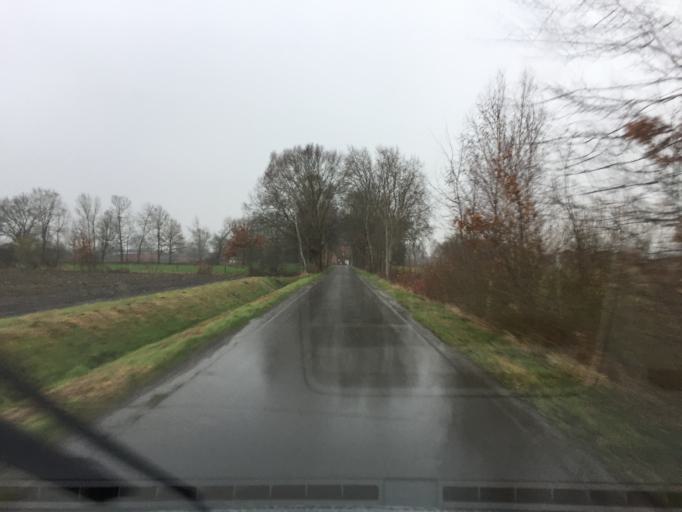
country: DE
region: Lower Saxony
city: Barenburg
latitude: 52.6473
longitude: 8.8332
